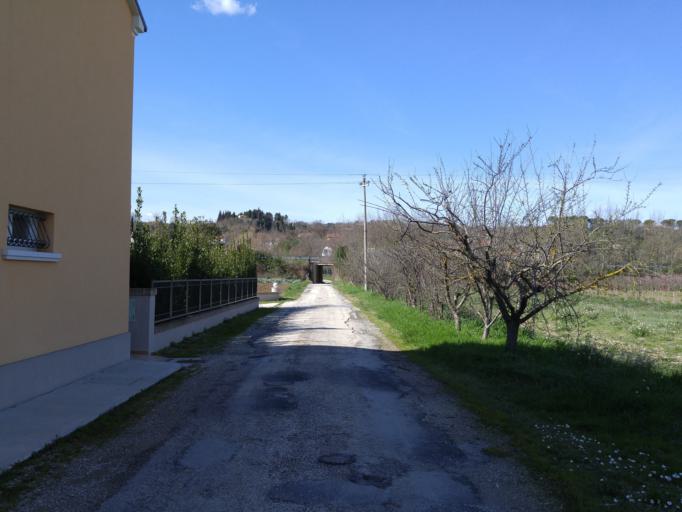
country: IT
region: The Marches
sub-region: Provincia di Pesaro e Urbino
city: Calcinelli
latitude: 43.7398
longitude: 12.9121
